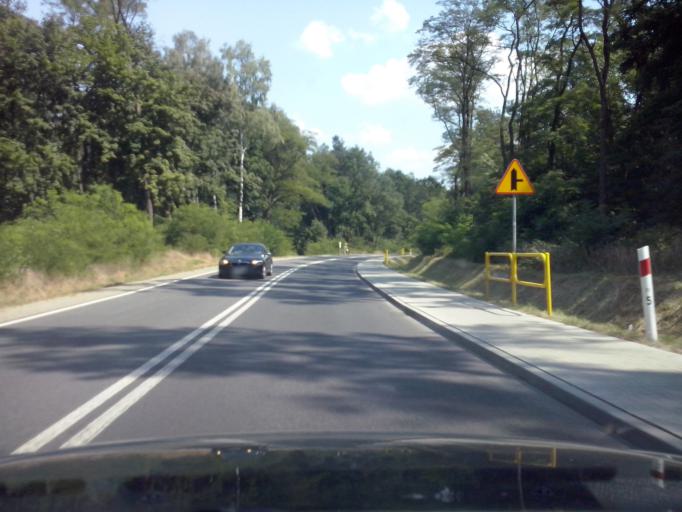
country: PL
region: Swietokrzyskie
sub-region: Powiat staszowski
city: Rytwiany
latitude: 50.5605
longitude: 21.2072
